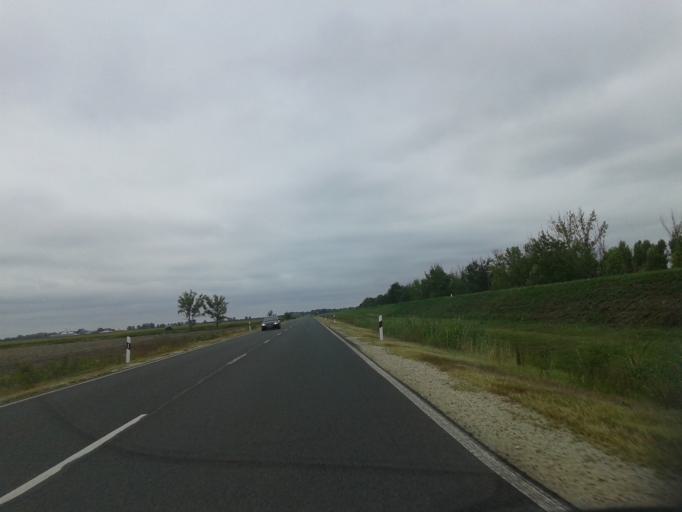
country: HU
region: Tolna
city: Bolcske
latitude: 46.7498
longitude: 19.0091
